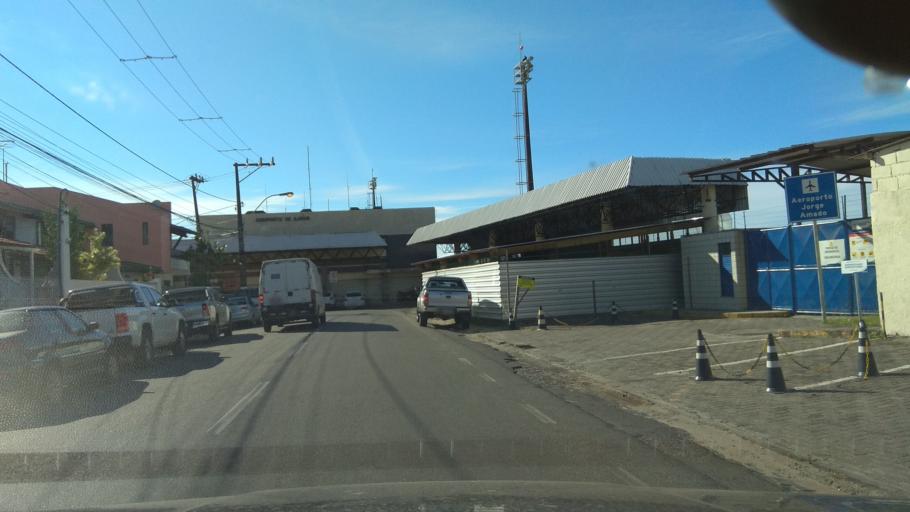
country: BR
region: Bahia
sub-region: Ilheus
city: Ilheus
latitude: -14.8141
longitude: -39.0327
